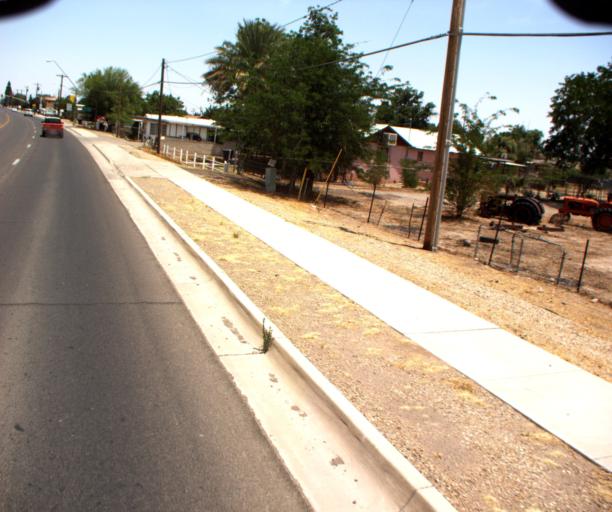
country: US
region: Arizona
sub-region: Graham County
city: Thatcher
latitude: 32.8491
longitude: -109.7702
